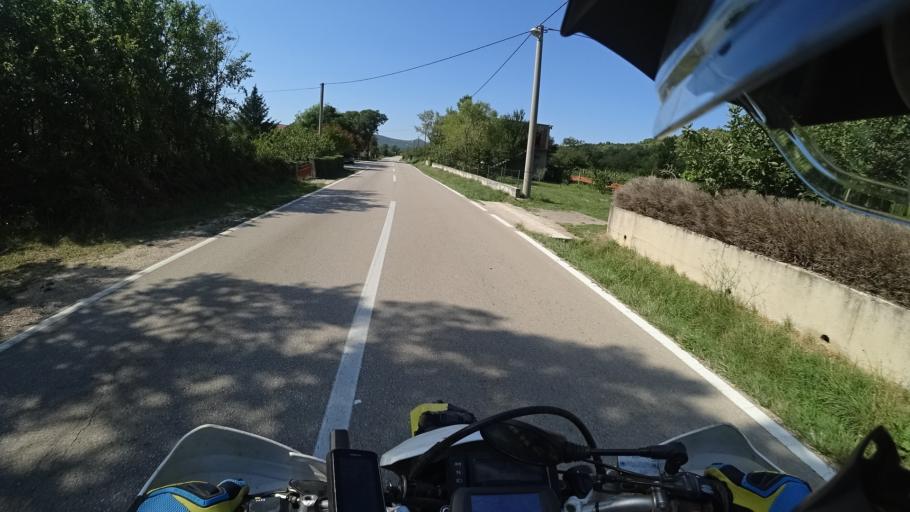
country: HR
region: Sibensko-Kniniska
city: Drnis
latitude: 43.8725
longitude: 16.1965
